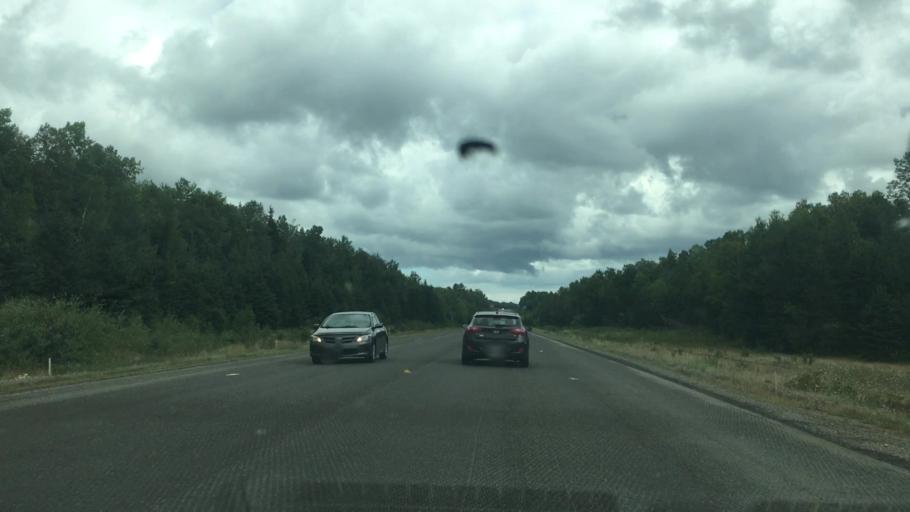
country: CA
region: Nova Scotia
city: Antigonish
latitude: 45.5872
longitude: -62.0789
